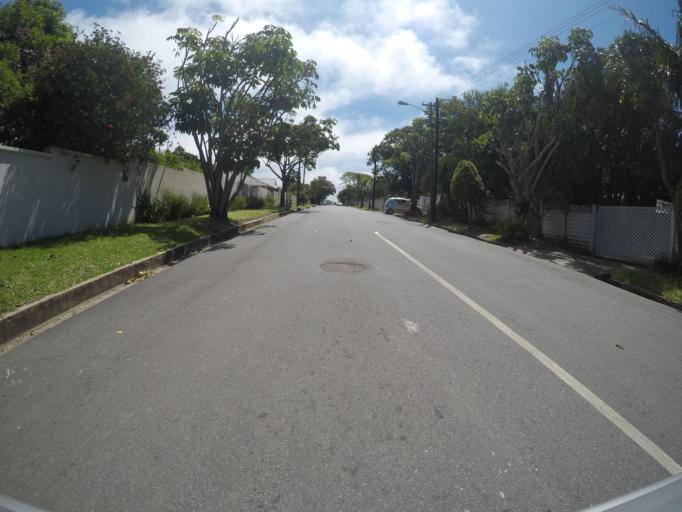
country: ZA
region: Eastern Cape
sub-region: Buffalo City Metropolitan Municipality
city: East London
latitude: -32.9749
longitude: 27.9017
